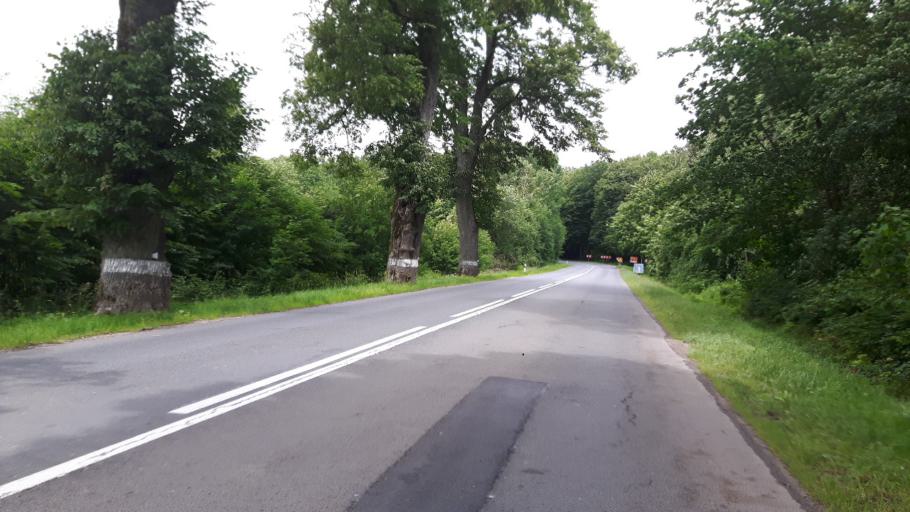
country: RU
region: Kaliningrad
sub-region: Zelenogradskiy Rayon
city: Zelenogradsk
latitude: 54.8261
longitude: 20.4294
